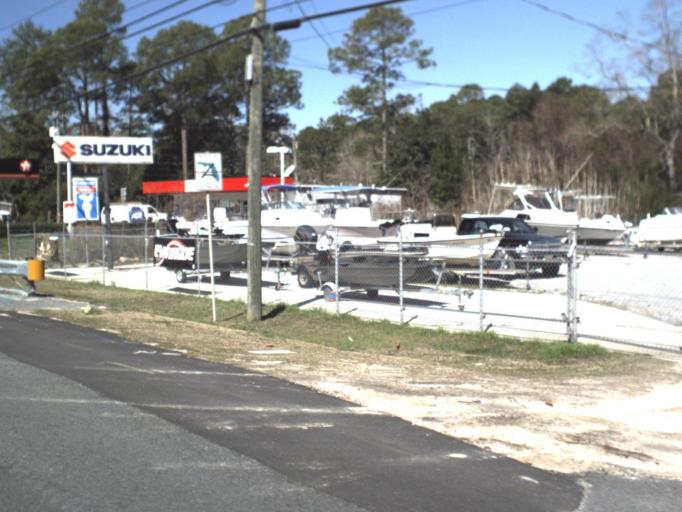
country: US
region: Florida
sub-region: Bay County
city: Callaway
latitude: 30.1529
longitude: -85.5649
